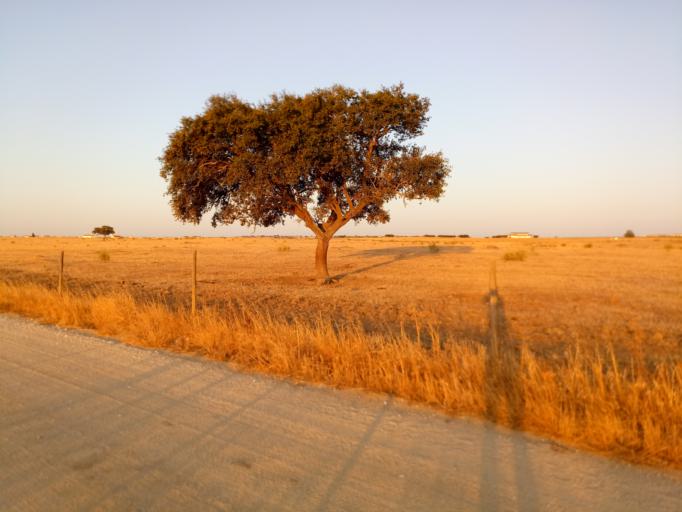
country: PT
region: Evora
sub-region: Reguengos de Monsaraz
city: Reguengos de Monsaraz
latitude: 38.3742
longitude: -7.4622
